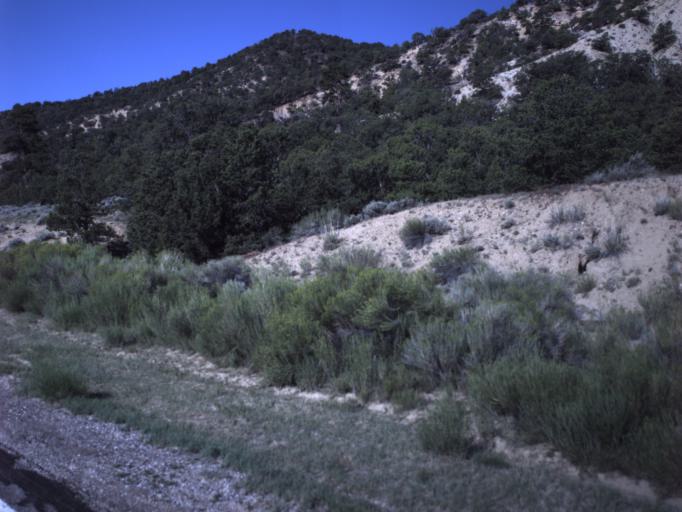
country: US
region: Utah
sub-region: Wayne County
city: Loa
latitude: 38.6680
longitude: -111.4247
